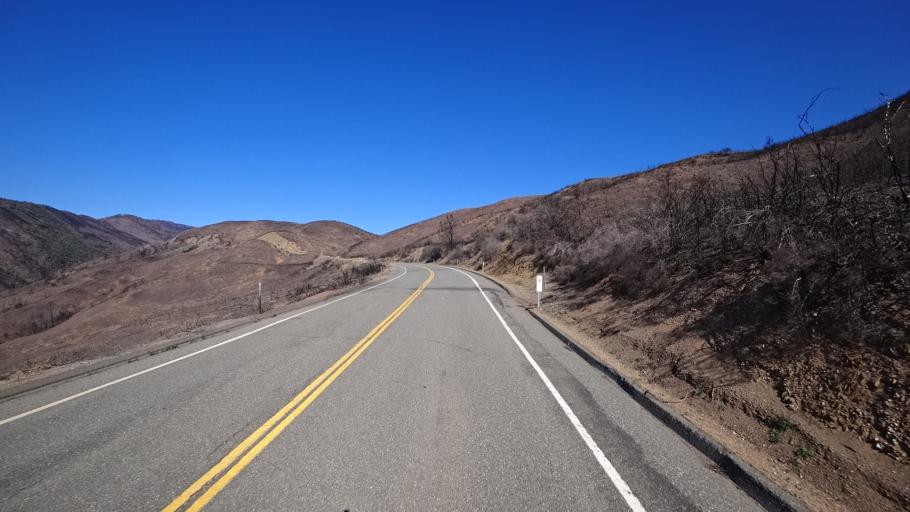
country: US
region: California
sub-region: Tehama County
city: Rancho Tehama Reserve
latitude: 39.6611
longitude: -122.6332
